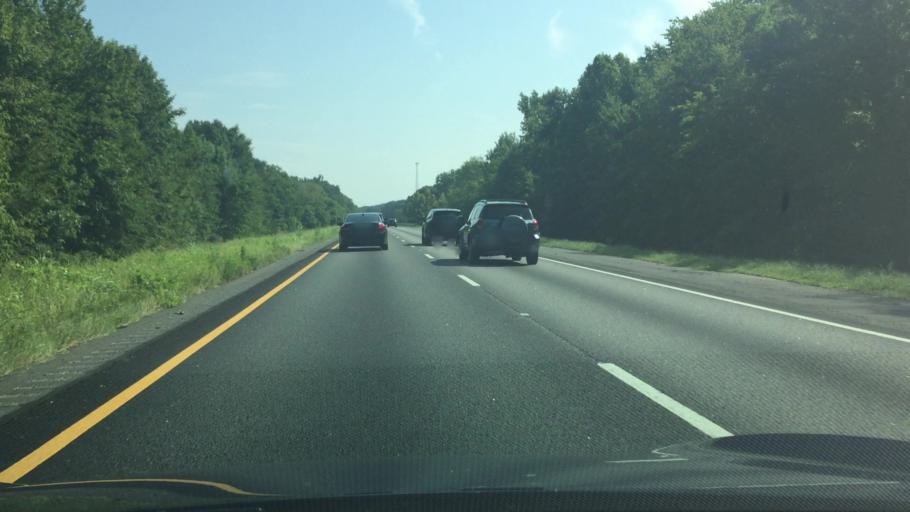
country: US
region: Alabama
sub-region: Montgomery County
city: Montgomery
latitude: 32.2247
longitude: -86.3914
